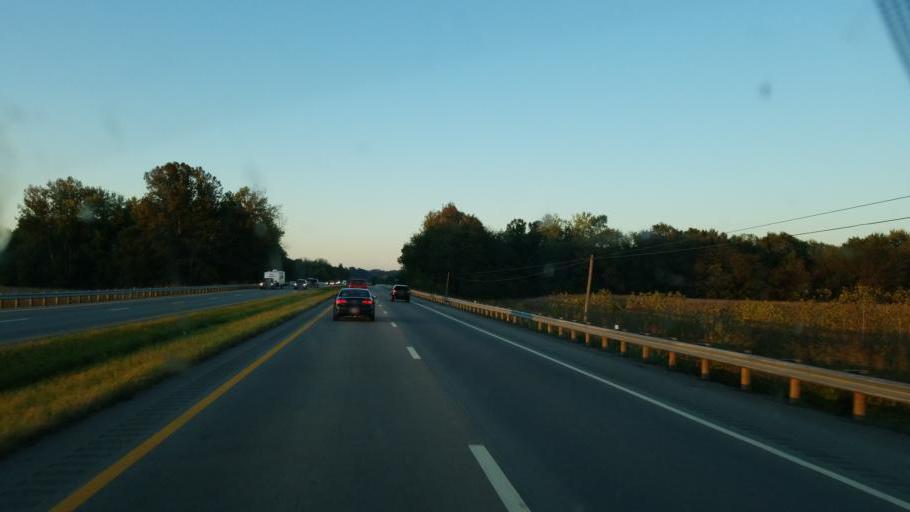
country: US
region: Ohio
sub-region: Pike County
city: Piketon
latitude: 39.0974
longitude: -83.0001
